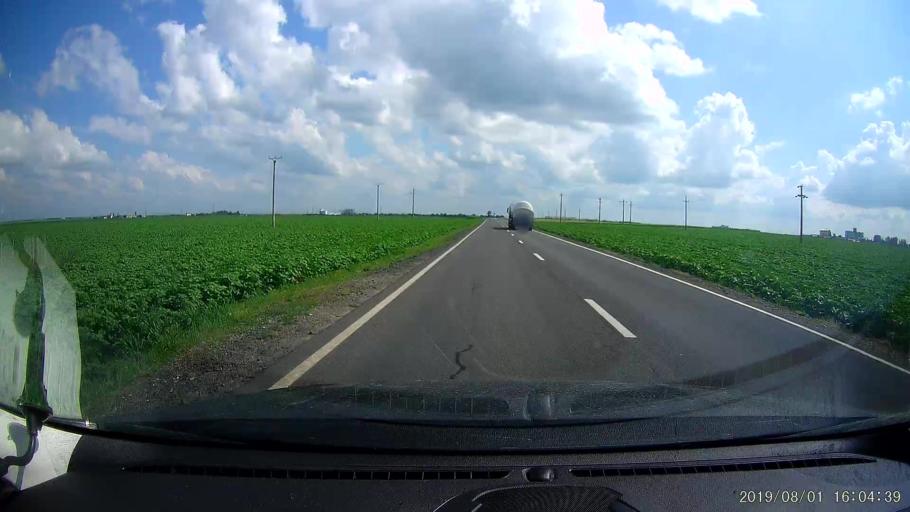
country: RO
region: Calarasi
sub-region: Comuna Dragalina
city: Drajna Noua
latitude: 44.4419
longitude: 27.3791
